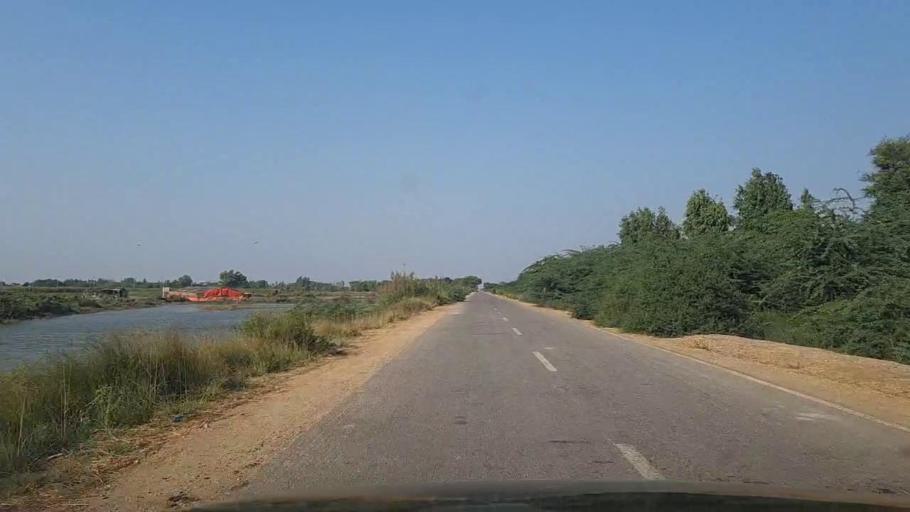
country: PK
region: Sindh
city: Thatta
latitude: 24.6186
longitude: 68.0517
